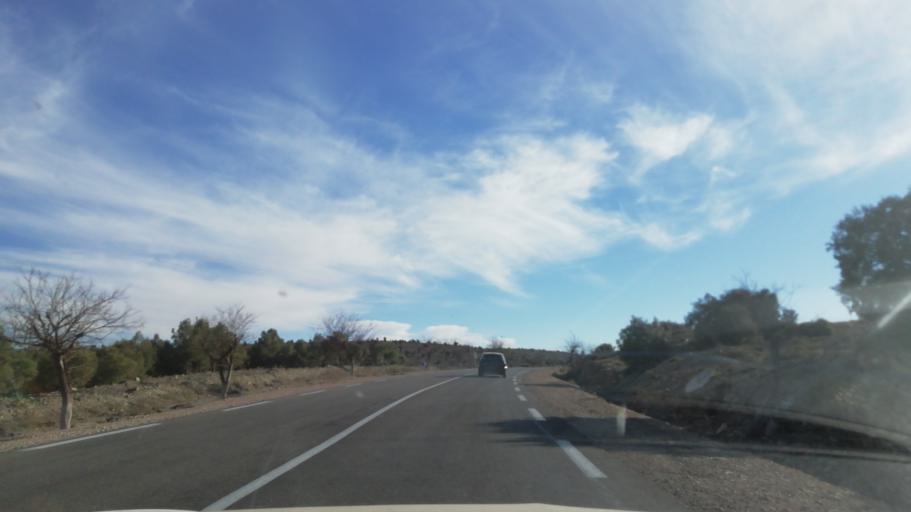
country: DZ
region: Tlemcen
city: Sebdou
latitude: 34.5875
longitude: -1.3176
